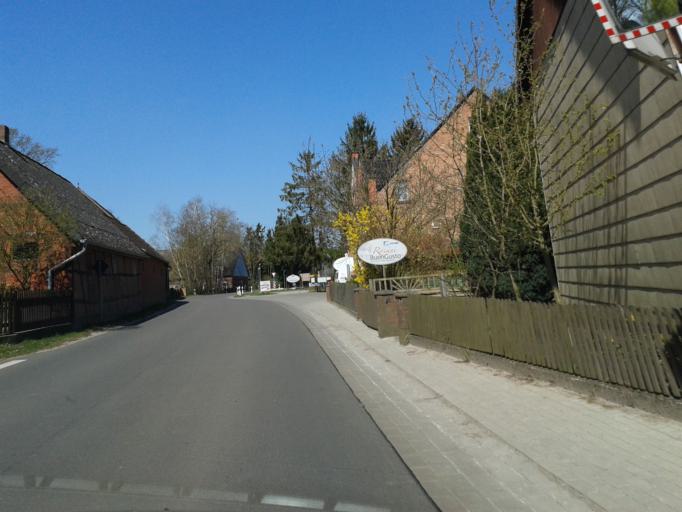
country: DE
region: Lower Saxony
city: Wustrow
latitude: 52.9363
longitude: 11.1174
